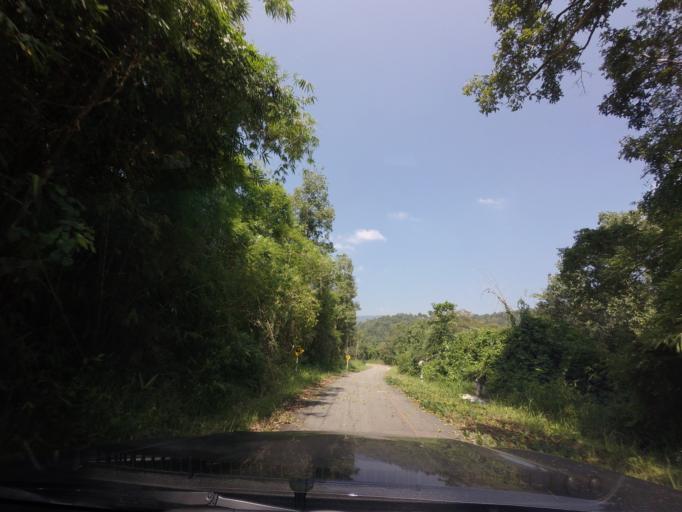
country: TH
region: Loei
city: Na Haeo
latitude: 17.5697
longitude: 100.9768
